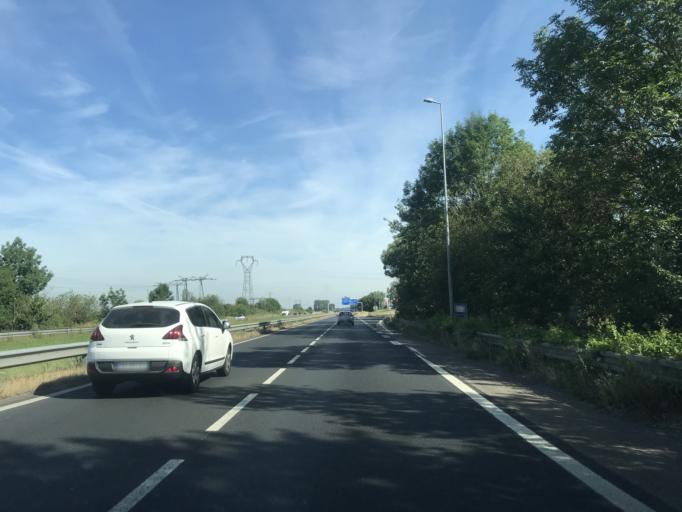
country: FR
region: Haute-Normandie
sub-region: Departement de la Seine-Maritime
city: La Vaupaliere
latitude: 49.4921
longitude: 0.9984
